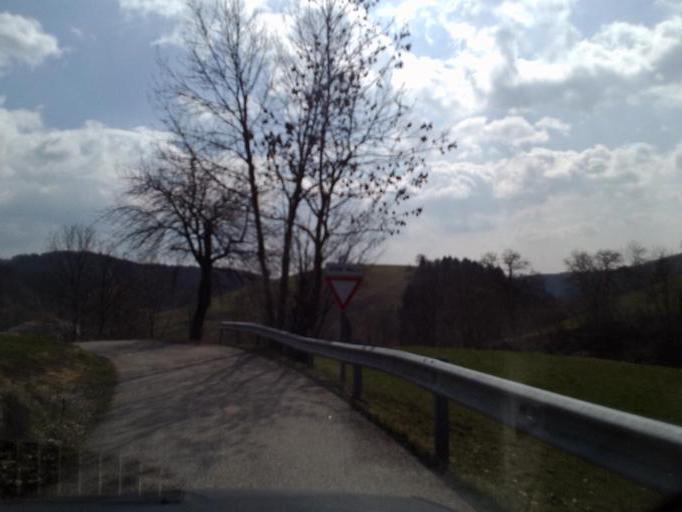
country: IT
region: Veneto
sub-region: Provincia di Verona
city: Erbezzo
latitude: 45.6501
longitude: 11.0178
